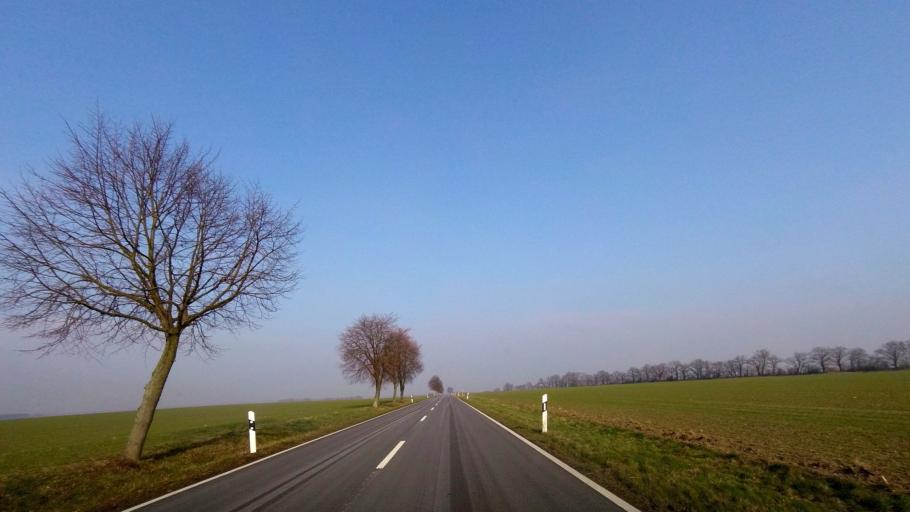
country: DE
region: Brandenburg
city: Niedergorsdorf
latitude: 51.9430
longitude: 13.0386
